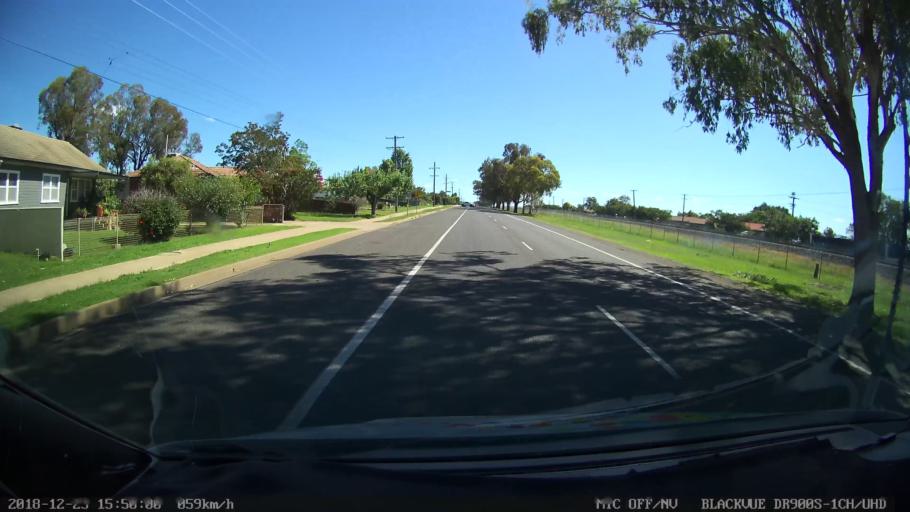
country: AU
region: New South Wales
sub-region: Tamworth Municipality
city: South Tamworth
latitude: -31.1030
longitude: 150.9031
